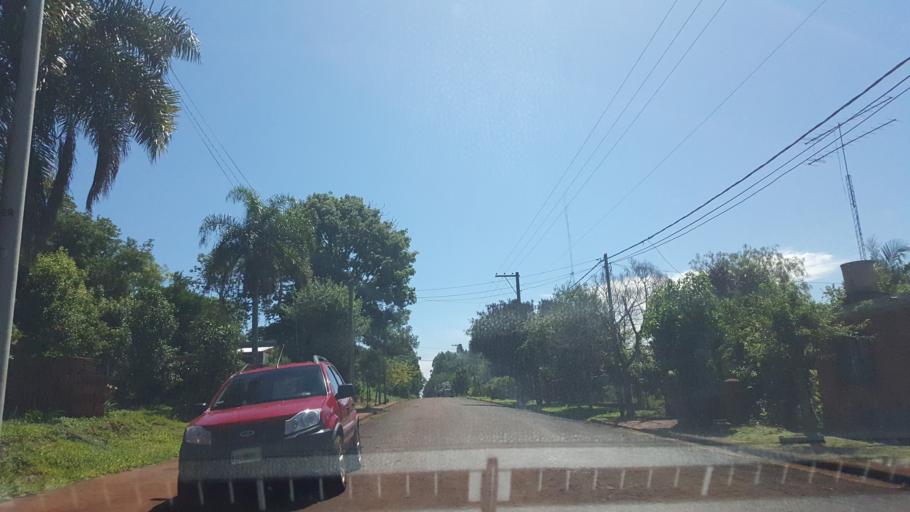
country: AR
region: Misiones
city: Capiovi
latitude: -26.9319
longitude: -55.0616
